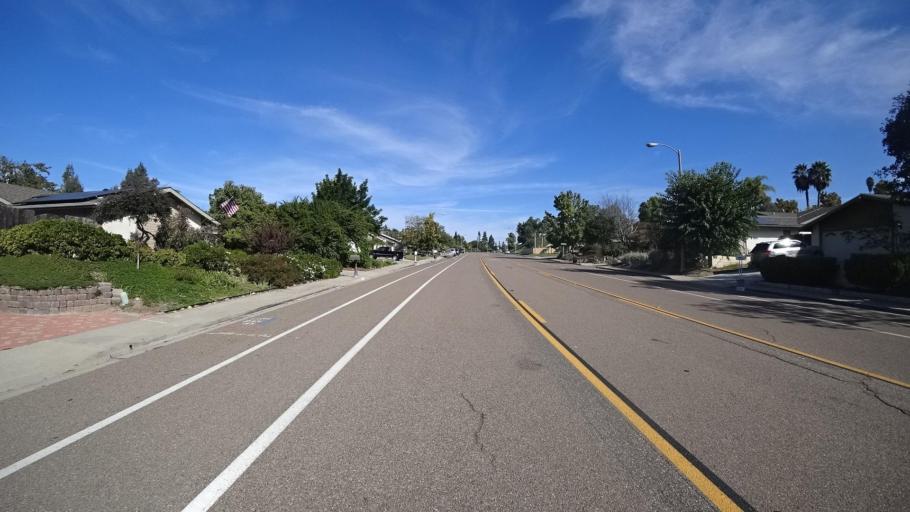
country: US
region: California
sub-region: San Diego County
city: Spring Valley
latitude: 32.7275
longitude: -116.9836
